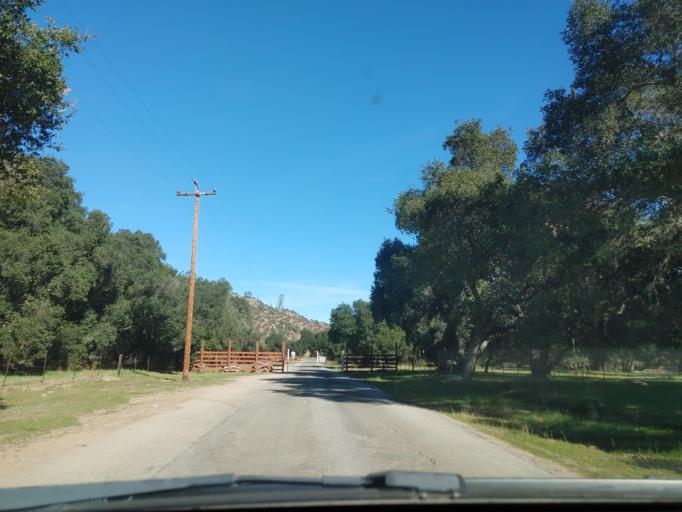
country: US
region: California
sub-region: San Benito County
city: Ridgemark
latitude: 36.6900
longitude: -121.3428
